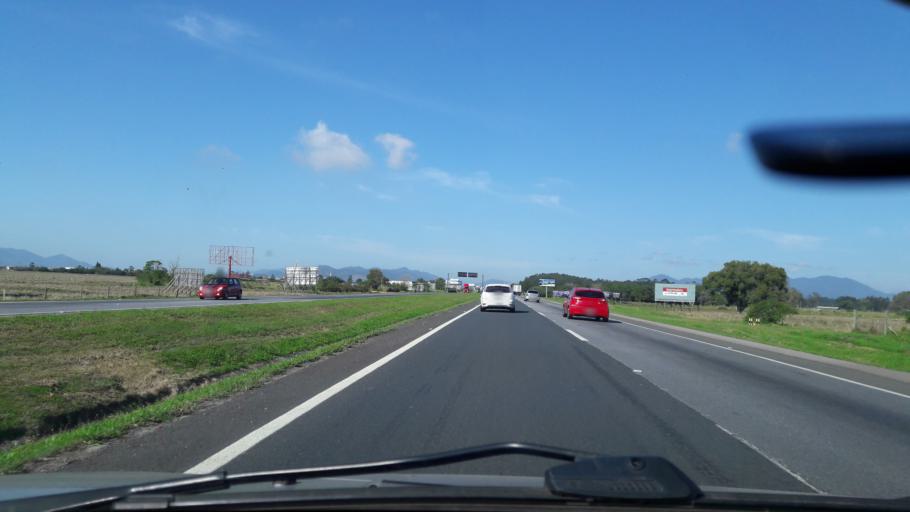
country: BR
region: Santa Catarina
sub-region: Tijucas
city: Tijucas
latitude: -27.2025
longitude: -48.6168
